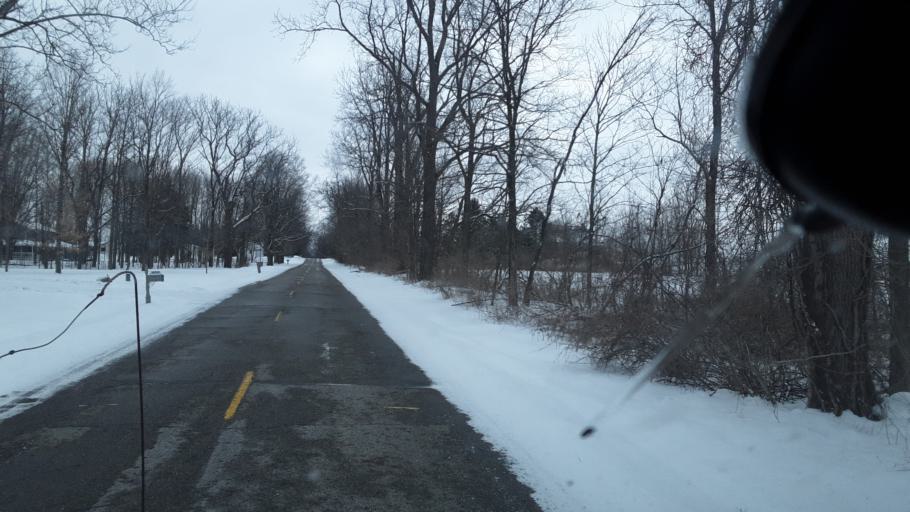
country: US
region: Michigan
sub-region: Ingham County
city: Mason
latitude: 42.5439
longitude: -84.4036
